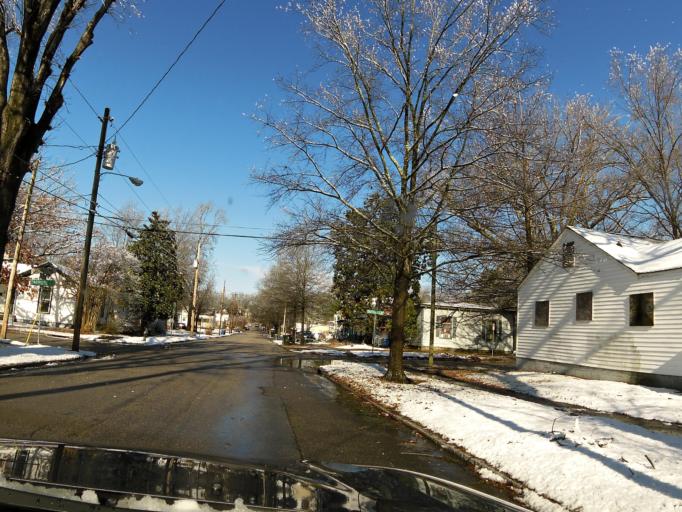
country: US
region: North Carolina
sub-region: Wilson County
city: Wilson
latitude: 35.7281
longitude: -77.9071
